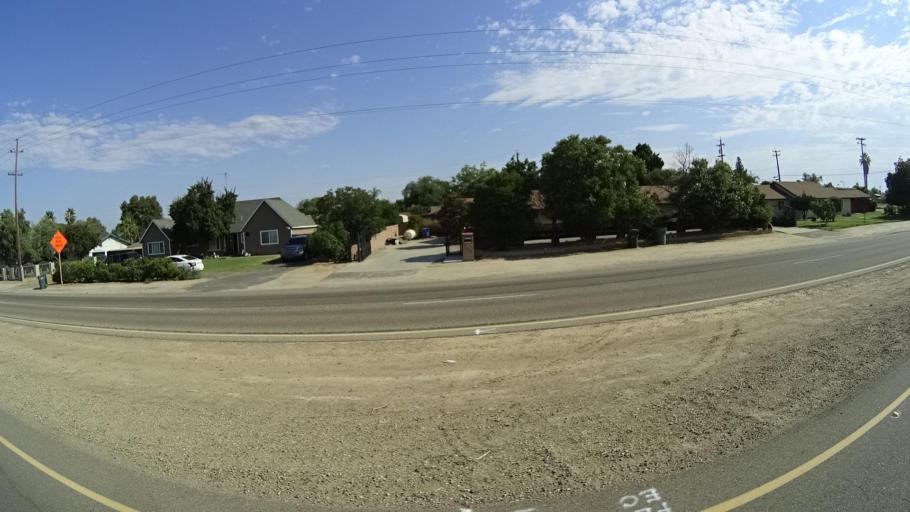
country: US
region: California
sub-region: Fresno County
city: Sunnyside
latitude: 36.7074
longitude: -119.6963
